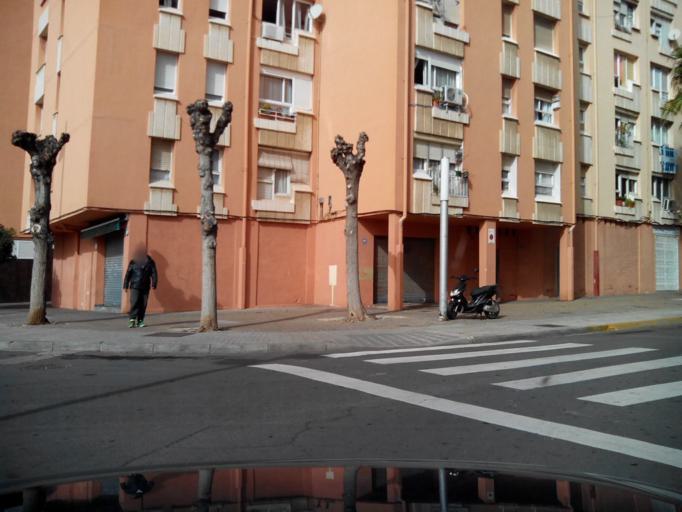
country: ES
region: Catalonia
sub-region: Provincia de Tarragona
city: Constanti
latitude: 41.1164
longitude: 1.2074
